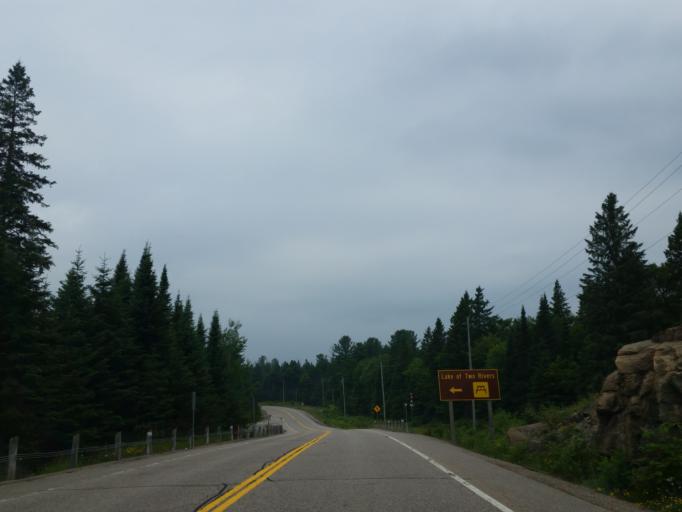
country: CA
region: Ontario
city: Mattawa
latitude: 45.5850
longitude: -78.4766
